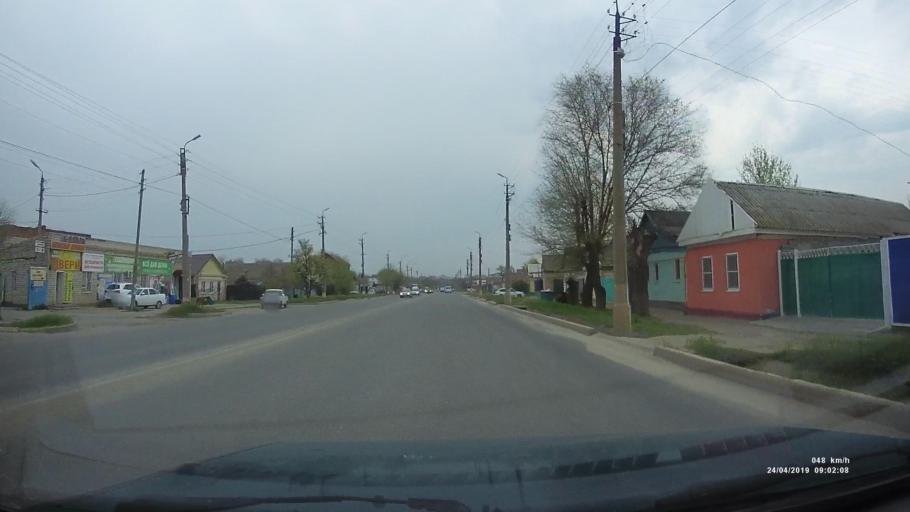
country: RU
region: Kalmykiya
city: Elista
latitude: 46.3123
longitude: 44.2308
